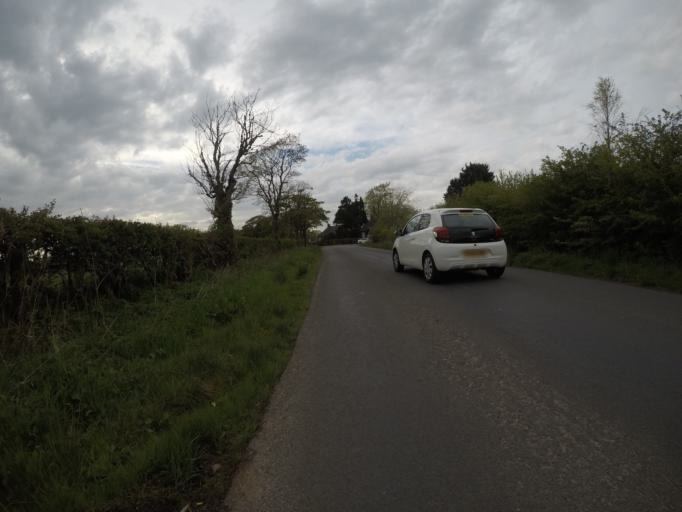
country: GB
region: Scotland
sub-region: East Ayrshire
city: Kilmarnock
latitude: 55.6453
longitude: -4.4841
